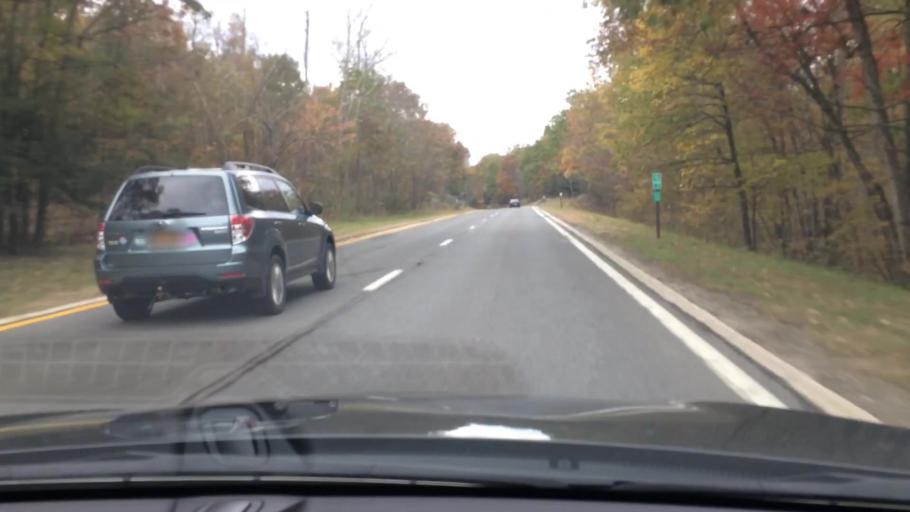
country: US
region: New York
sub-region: Dutchess County
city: Pine Plains
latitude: 42.0515
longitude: -73.7325
